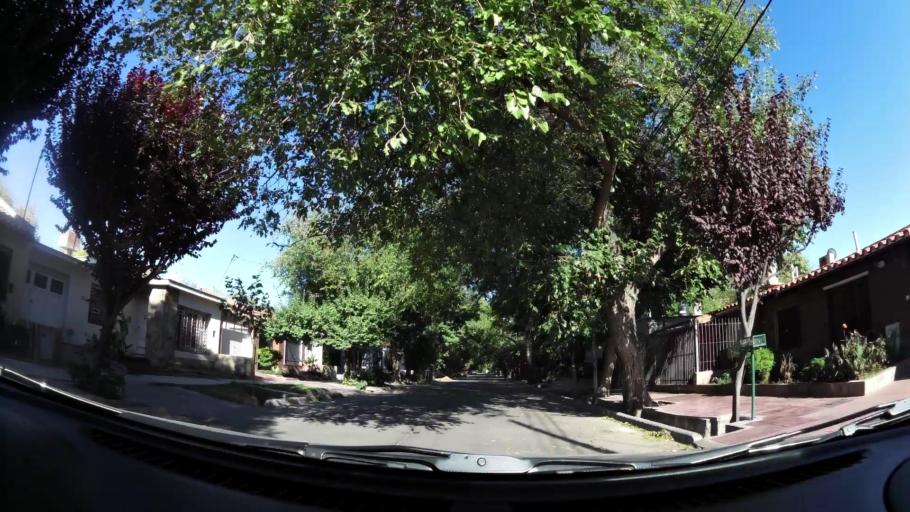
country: AR
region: Mendoza
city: Las Heras
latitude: -32.8633
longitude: -68.8440
